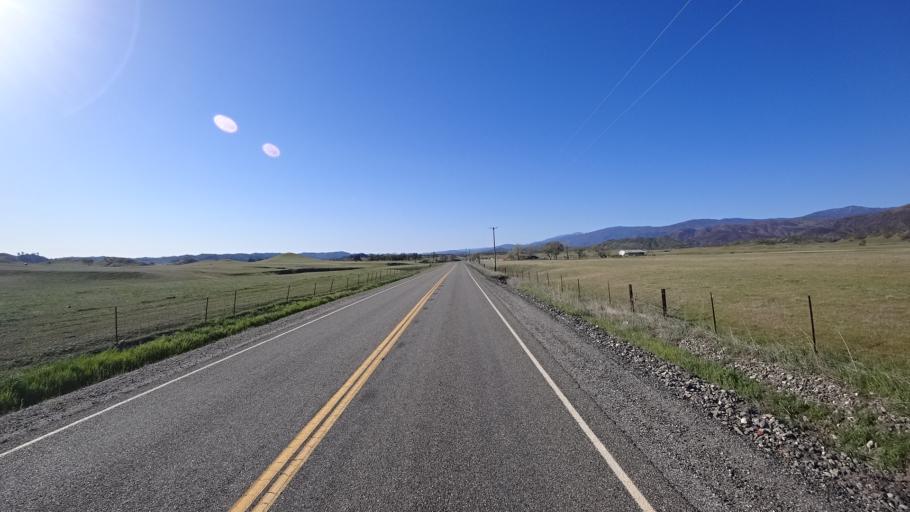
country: US
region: California
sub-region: Tehama County
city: Rancho Tehama Reserve
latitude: 39.7056
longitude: -122.5504
